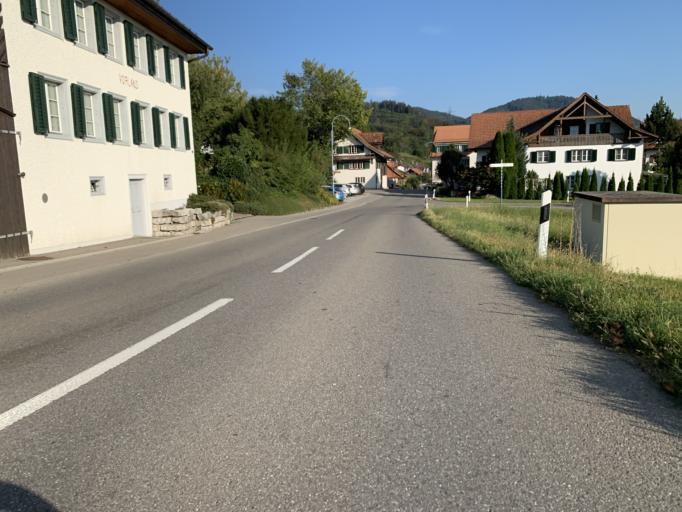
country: CH
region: Zurich
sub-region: Bezirk Hinwil
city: Baretswil
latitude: 47.3165
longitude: 8.8523
